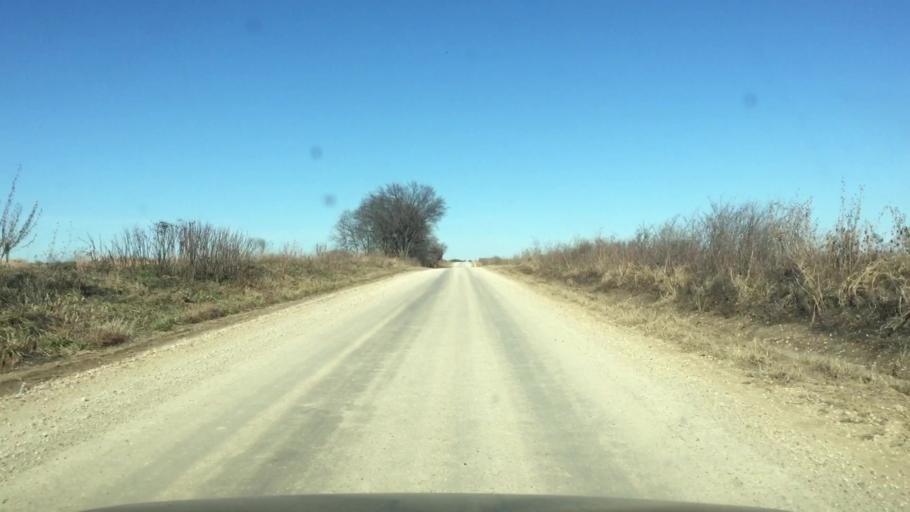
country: US
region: Kansas
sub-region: Allen County
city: Humboldt
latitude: 37.8561
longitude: -95.3910
